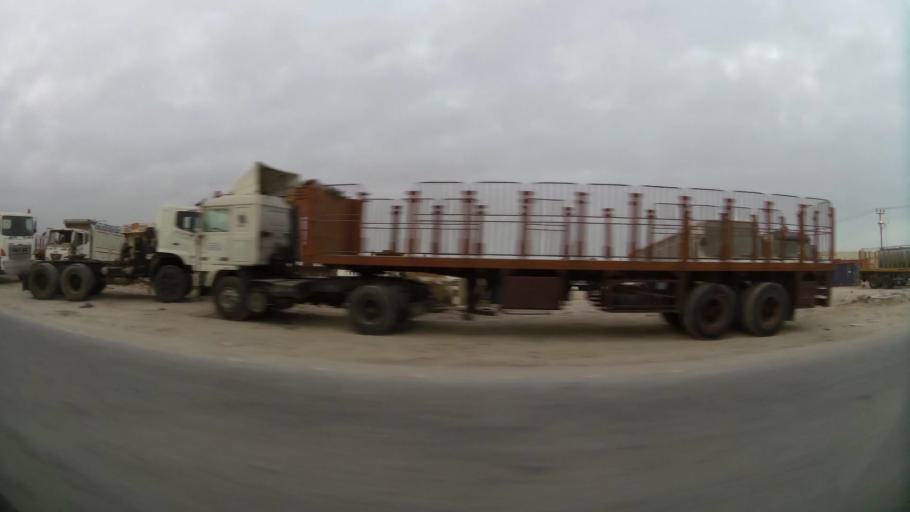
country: OM
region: Zufar
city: Salalah
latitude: 17.0256
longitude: 54.0425
